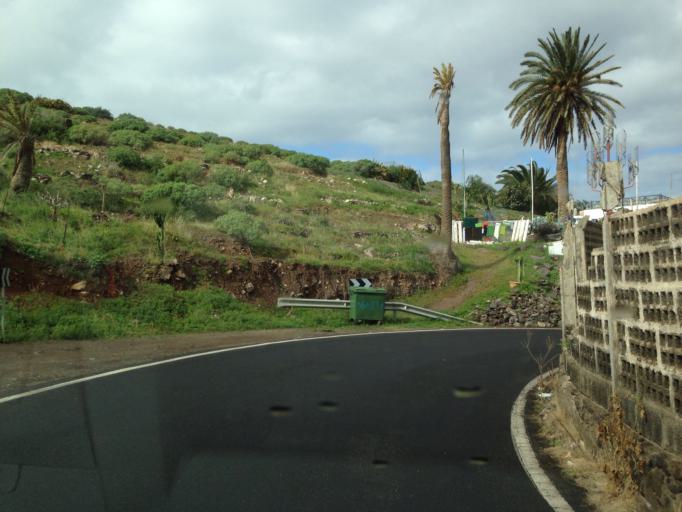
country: ES
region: Canary Islands
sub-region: Provincia de Las Palmas
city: Agaete
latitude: 28.0980
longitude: -15.7036
